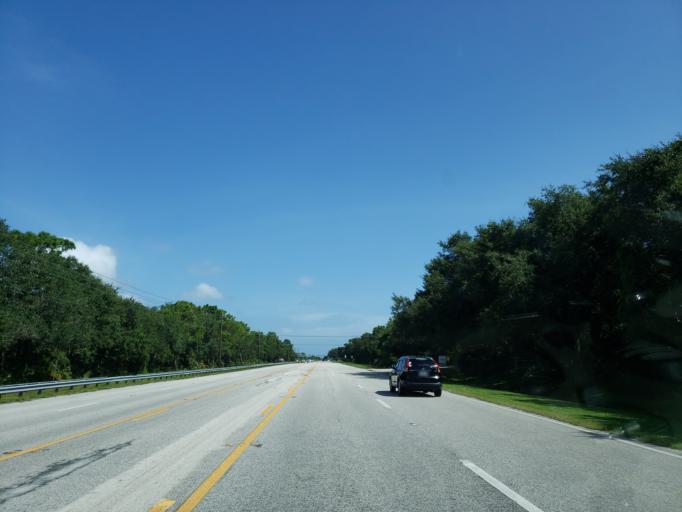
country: US
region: Florida
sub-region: Brevard County
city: West Melbourne
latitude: 28.0880
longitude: -80.6547
